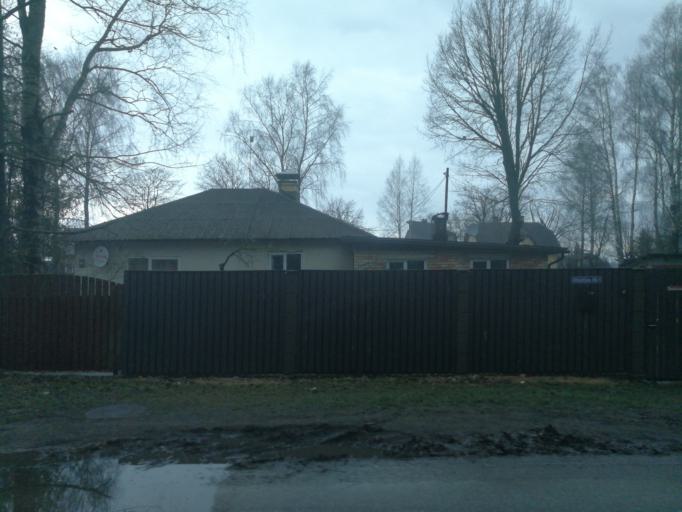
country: LV
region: Riga
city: Bolderaja
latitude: 57.0483
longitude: 24.0970
